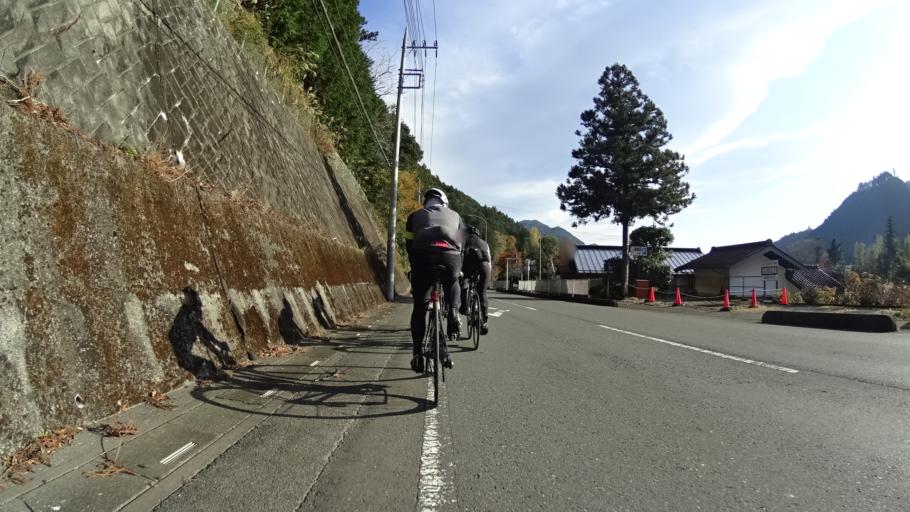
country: JP
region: Tokyo
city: Ome
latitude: 35.8884
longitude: 139.1803
